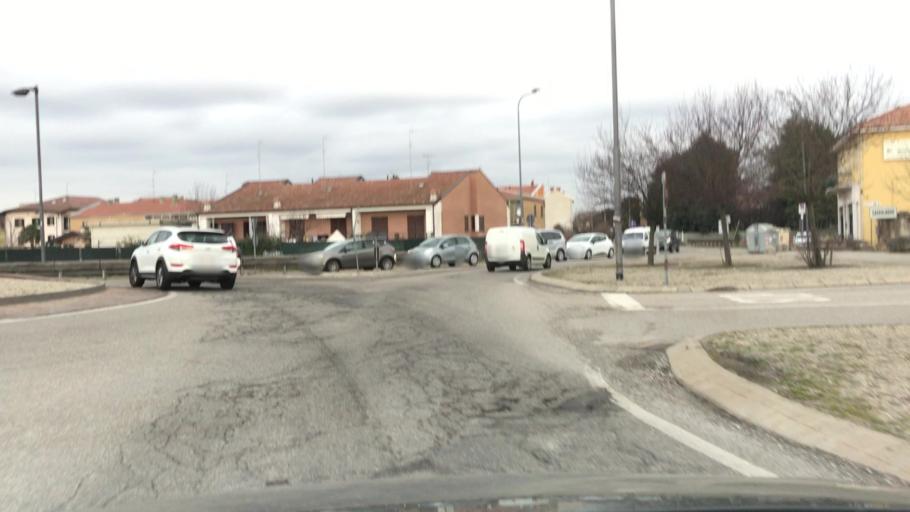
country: IT
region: Lombardy
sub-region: Provincia di Pavia
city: Cassolnovo
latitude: 45.3566
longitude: 8.8141
